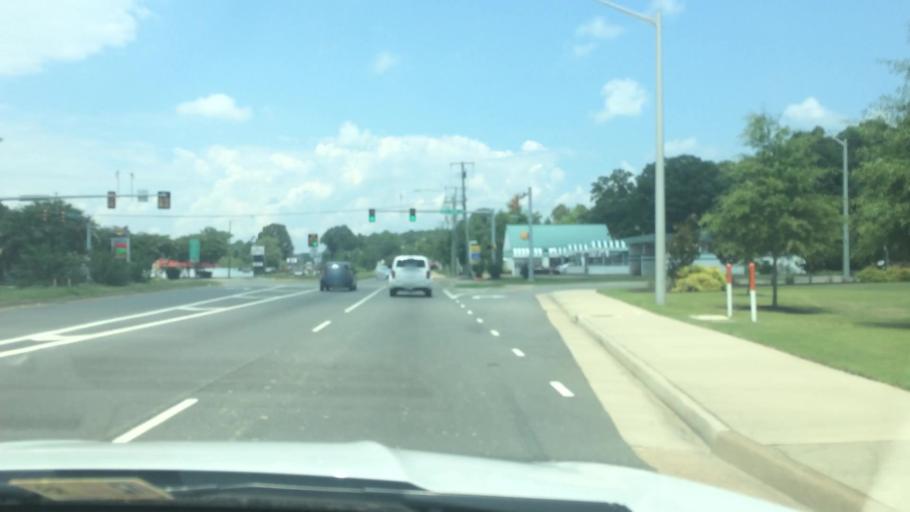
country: US
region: Virginia
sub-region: York County
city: Yorktown
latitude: 37.1429
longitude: -76.5480
